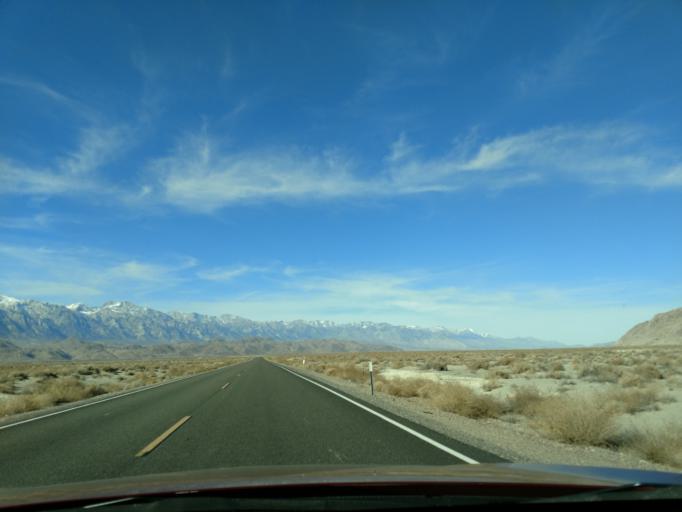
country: US
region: California
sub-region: Inyo County
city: Lone Pine
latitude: 36.5663
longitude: -117.9799
